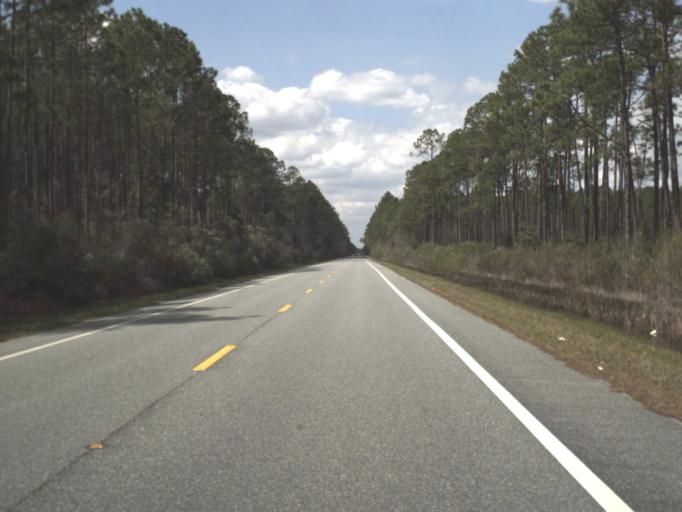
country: US
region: Florida
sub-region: Franklin County
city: Eastpoint
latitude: 29.8386
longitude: -84.9376
